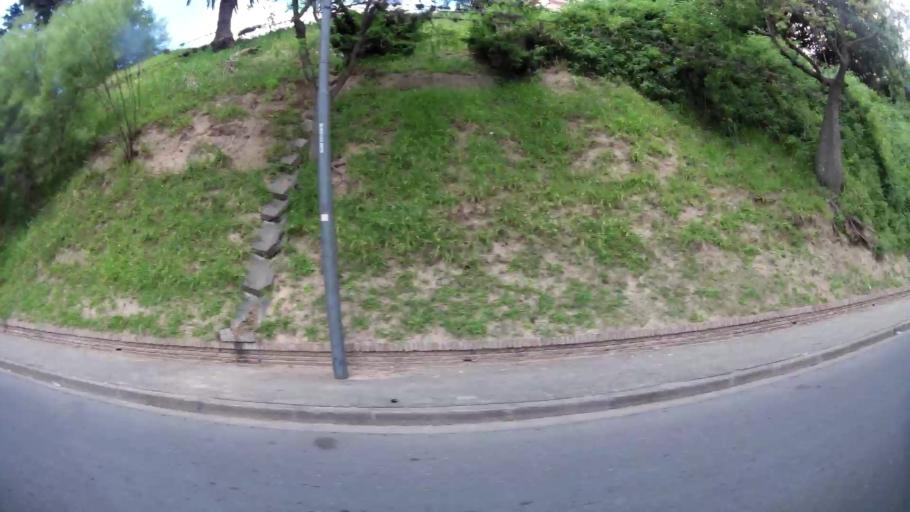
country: AR
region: Santa Fe
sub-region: Departamento de Rosario
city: Rosario
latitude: -32.9546
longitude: -60.6236
